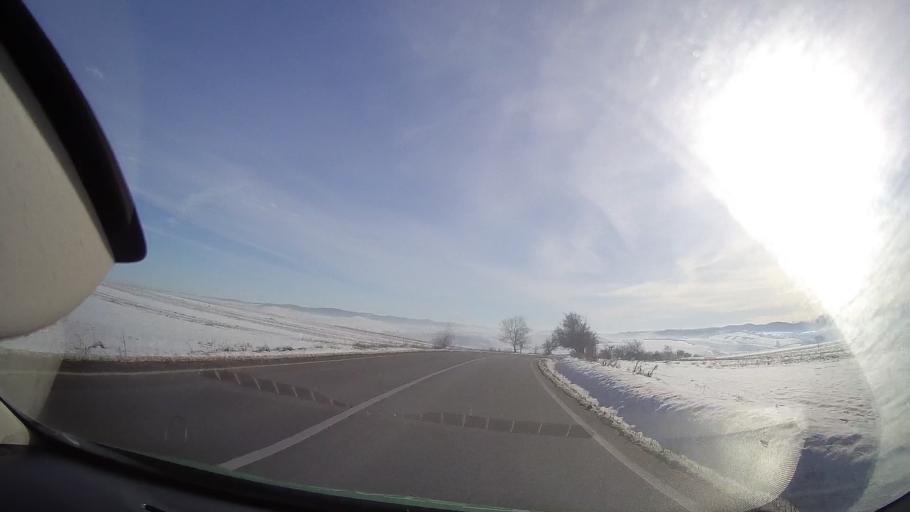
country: RO
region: Neamt
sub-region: Comuna Baltatesti
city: Valea Seaca
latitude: 47.1549
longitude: 26.3240
